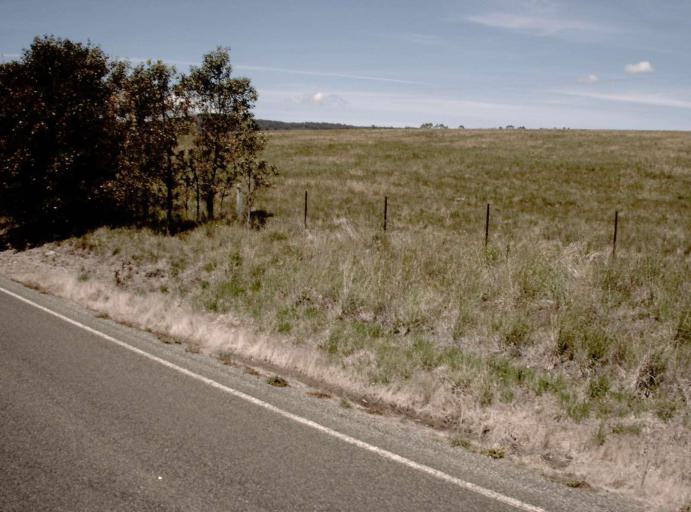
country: AU
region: Victoria
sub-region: Alpine
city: Mount Beauty
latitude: -37.1437
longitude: 147.6472
